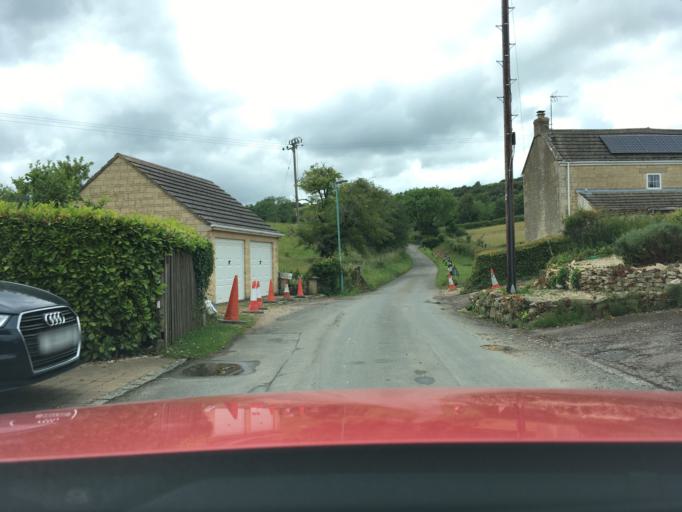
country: GB
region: England
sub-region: Gloucestershire
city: Winchcombe
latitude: 51.9518
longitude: -1.9789
